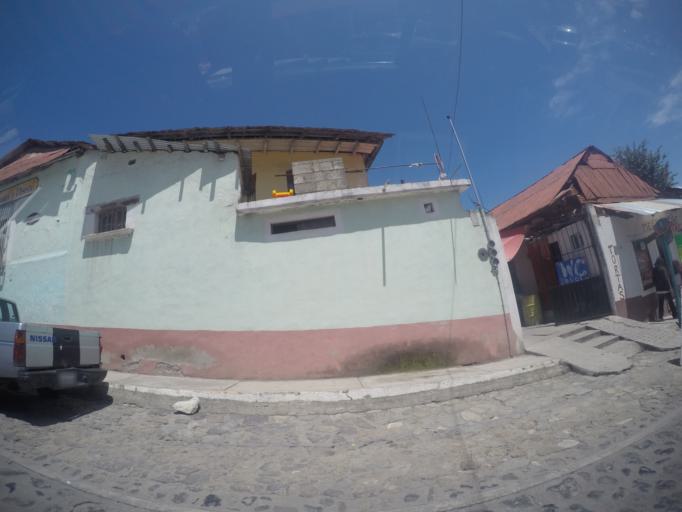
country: MX
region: Hidalgo
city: Mineral del Monte
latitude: 20.1359
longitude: -98.6711
